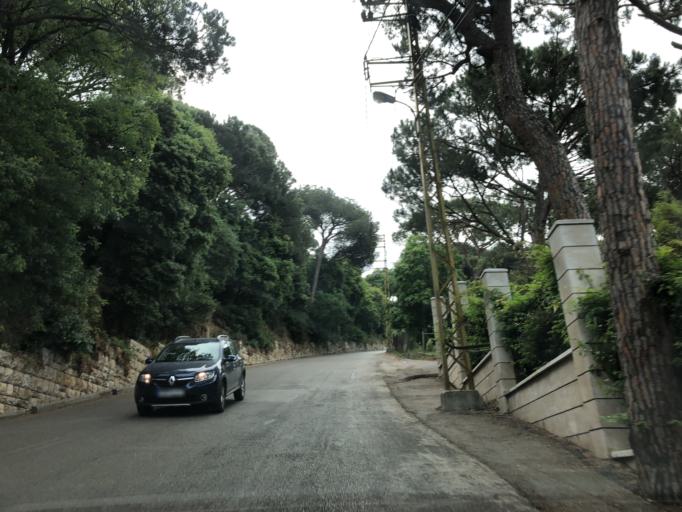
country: LB
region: Mont-Liban
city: Jdaidet el Matn
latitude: 33.8592
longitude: 35.5998
